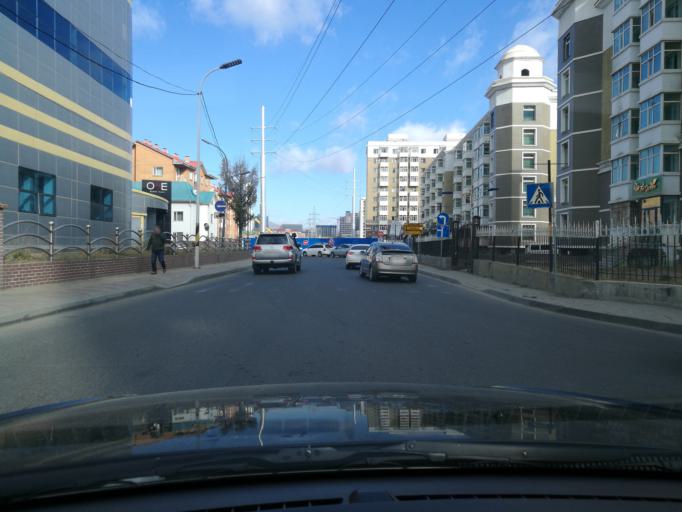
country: MN
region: Ulaanbaatar
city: Ulaanbaatar
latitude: 47.9043
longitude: 106.9282
